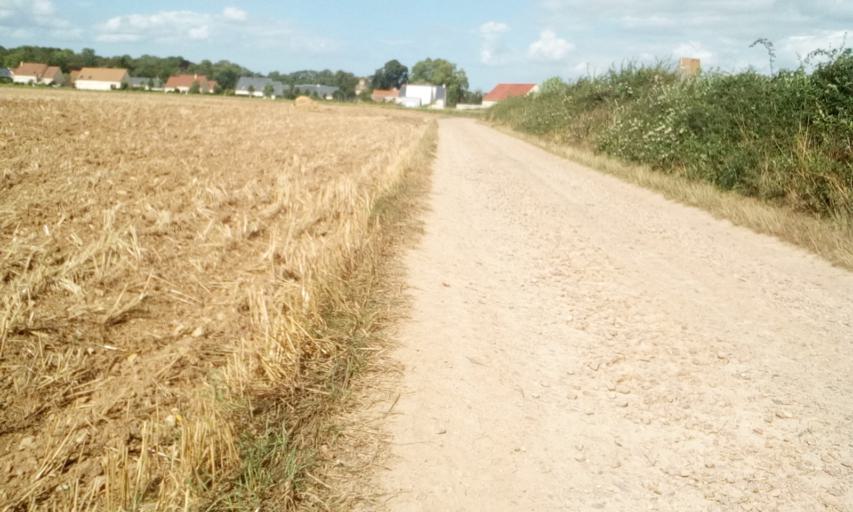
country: FR
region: Lower Normandy
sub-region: Departement du Calvados
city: Bellengreville
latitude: 49.1078
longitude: -0.2253
